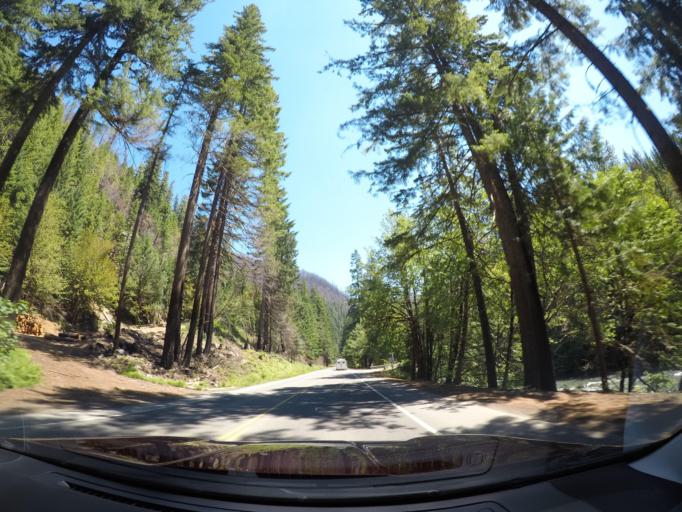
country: US
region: Oregon
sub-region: Linn County
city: Mill City
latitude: 44.6914
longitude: -121.9886
